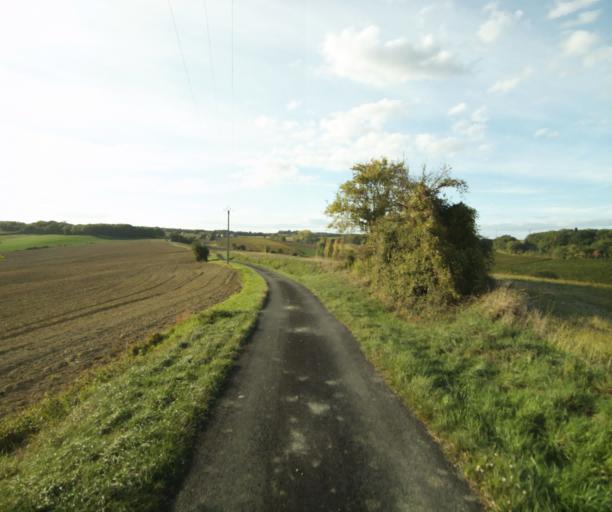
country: FR
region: Midi-Pyrenees
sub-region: Departement du Gers
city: Gondrin
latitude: 43.8884
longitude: 0.2671
